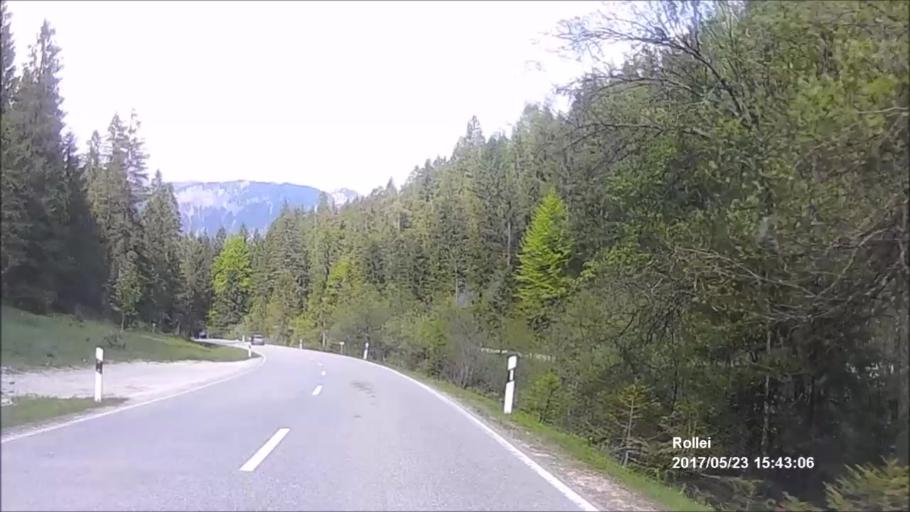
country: DE
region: Bavaria
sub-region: Upper Bavaria
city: Ramsau
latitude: 47.6415
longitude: 12.9154
